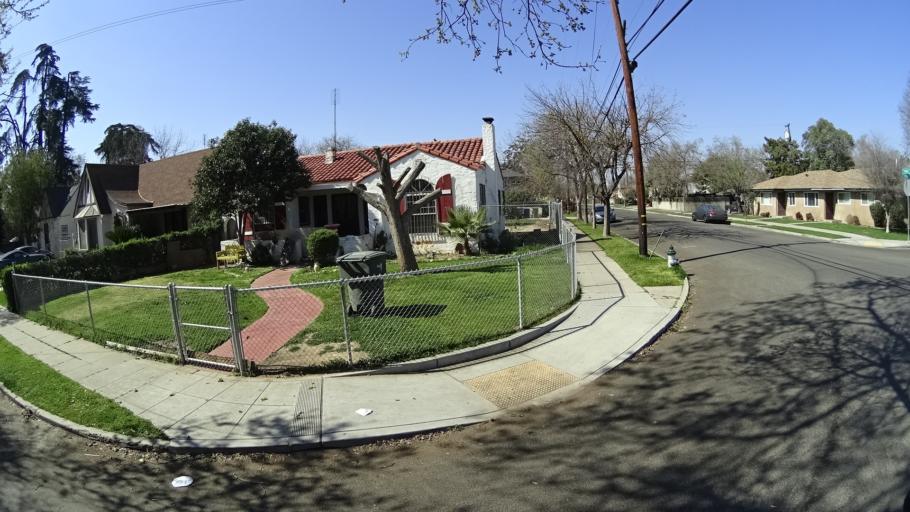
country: US
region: California
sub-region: Fresno County
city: Fresno
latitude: 36.7521
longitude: -119.8017
